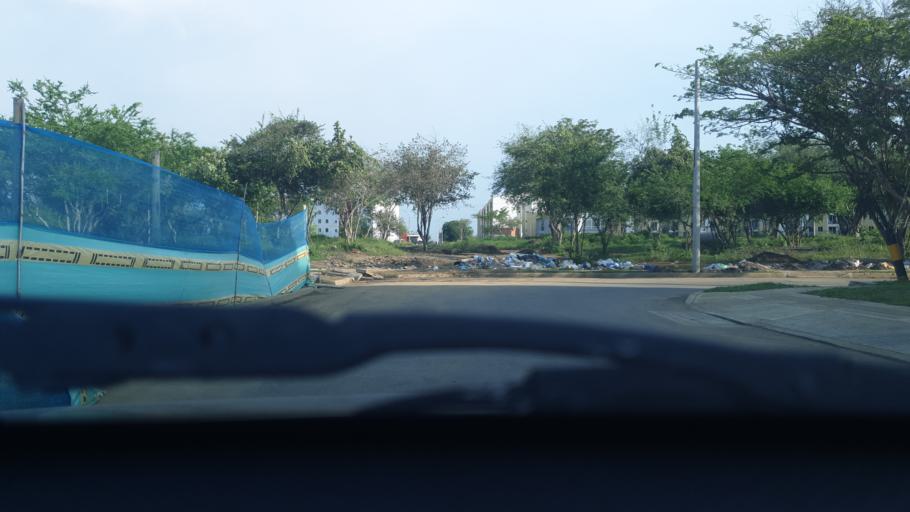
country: CO
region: Valle del Cauca
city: Jamundi
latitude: 3.3471
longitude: -76.5138
